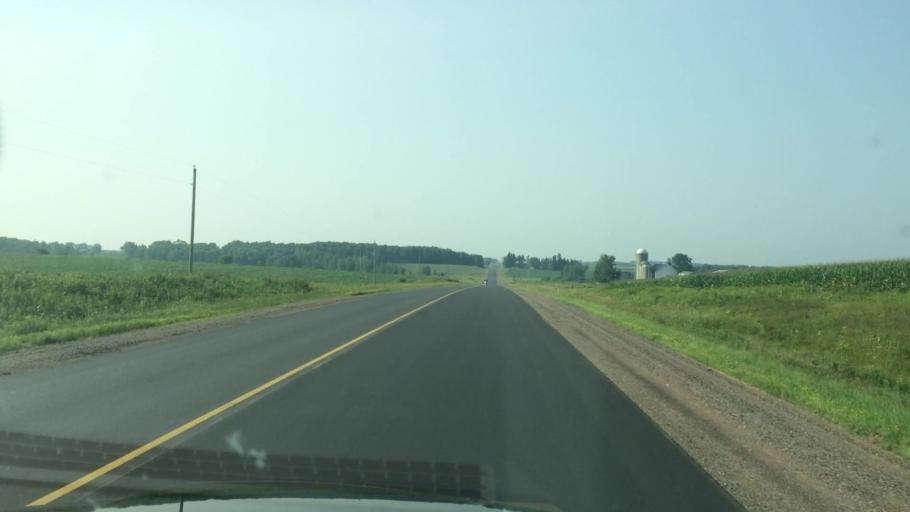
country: US
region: Wisconsin
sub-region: Marathon County
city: Athens
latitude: 44.9198
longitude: -90.0787
